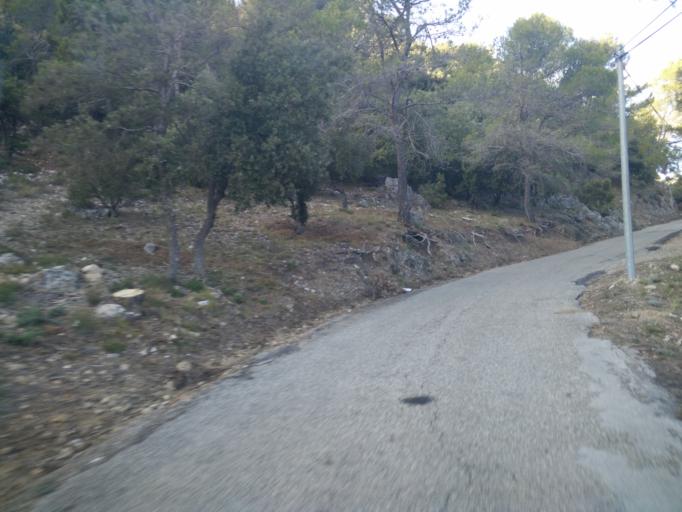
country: FR
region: Provence-Alpes-Cote d'Azur
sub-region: Departement du Var
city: Belgentier
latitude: 43.2164
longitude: 5.9814
